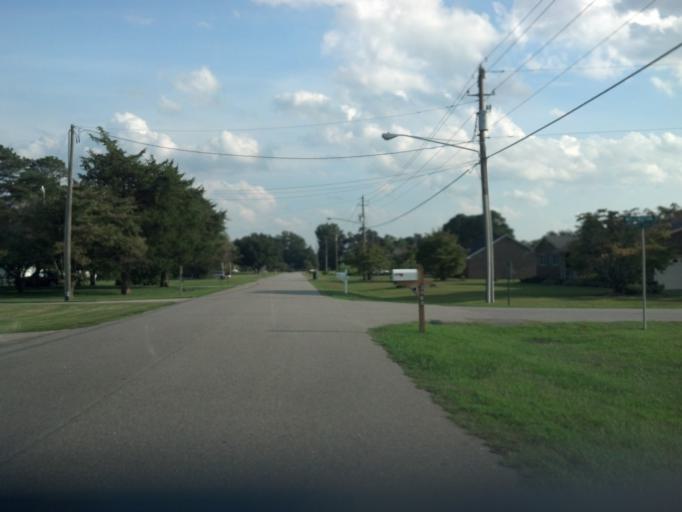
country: US
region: North Carolina
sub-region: Pitt County
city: Ayden
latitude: 35.4792
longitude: -77.4102
